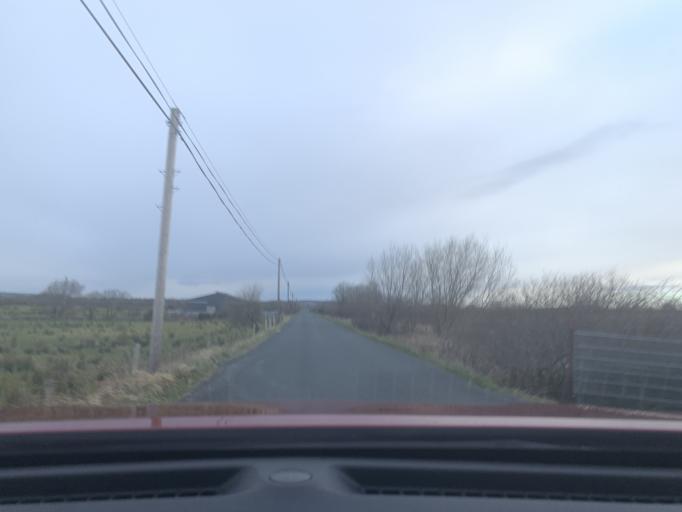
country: IE
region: Connaught
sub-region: Roscommon
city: Ballaghaderreen
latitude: 53.8879
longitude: -8.5700
